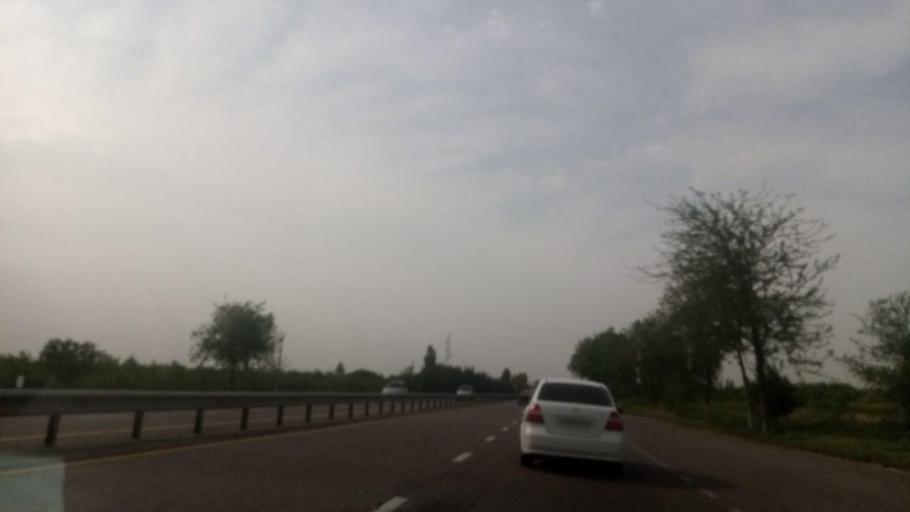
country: UZ
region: Toshkent
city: Tuytepa
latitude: 41.1143
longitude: 69.4463
